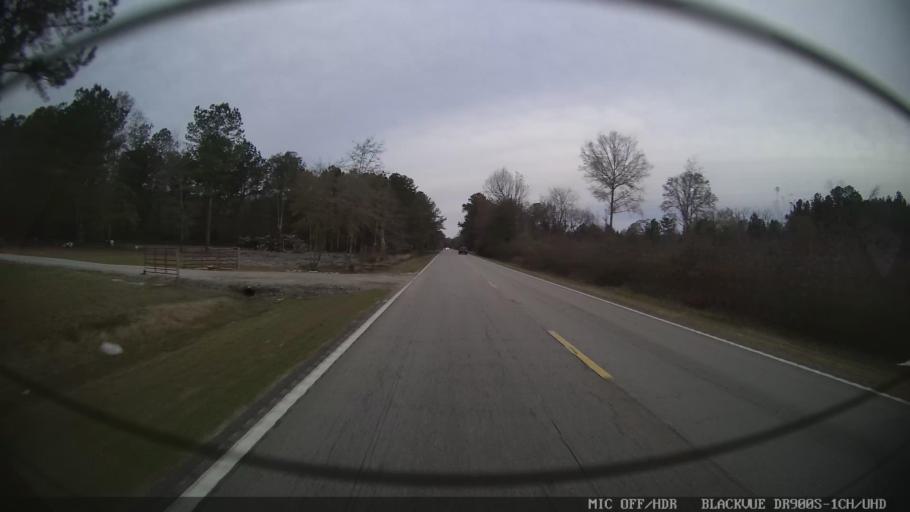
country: US
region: Mississippi
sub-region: Clarke County
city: Stonewall
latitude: 32.0347
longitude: -88.8733
